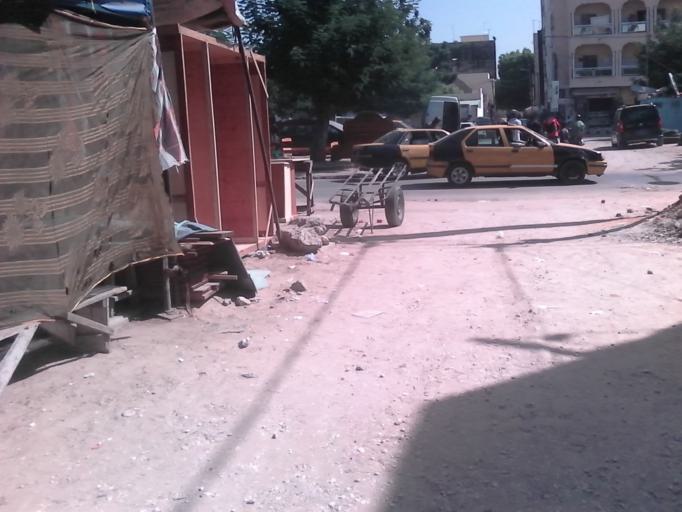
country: SN
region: Dakar
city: Grand Dakar
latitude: 14.7078
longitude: -17.4533
